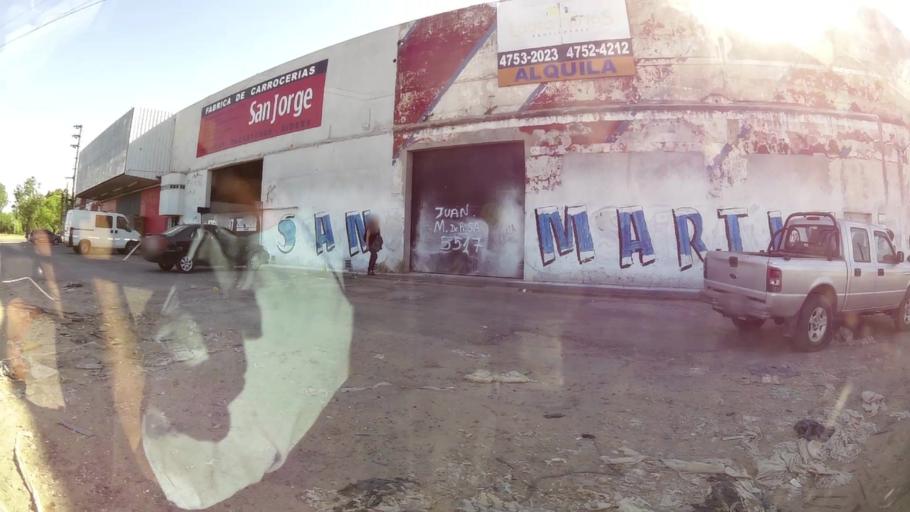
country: AR
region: Buenos Aires
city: Caseros
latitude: -34.5587
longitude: -58.5874
